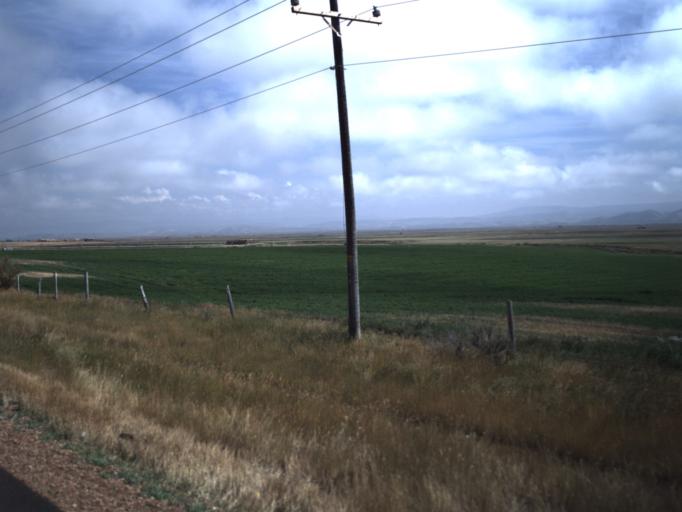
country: US
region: Utah
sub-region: Rich County
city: Randolph
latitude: 41.7374
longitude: -111.1564
